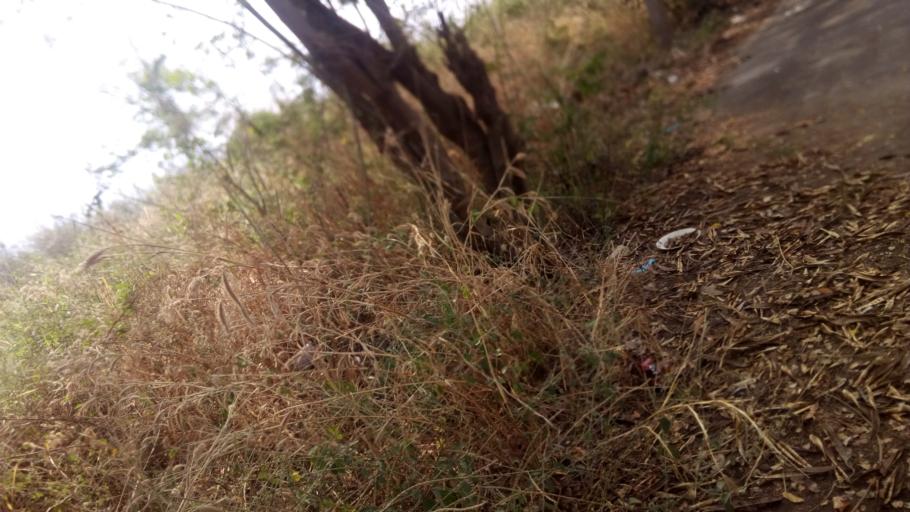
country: TH
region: Pathum Thani
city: Nong Suea
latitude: 14.0514
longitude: 100.8469
